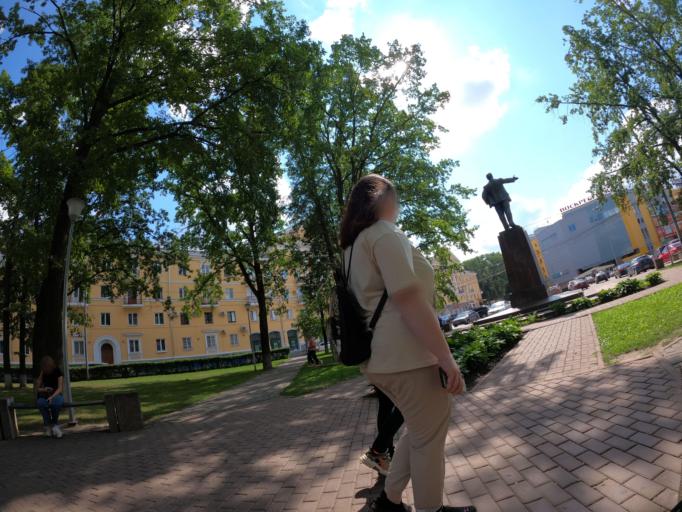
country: RU
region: Moskovskaya
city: Voskresensk
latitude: 55.3230
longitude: 38.6733
